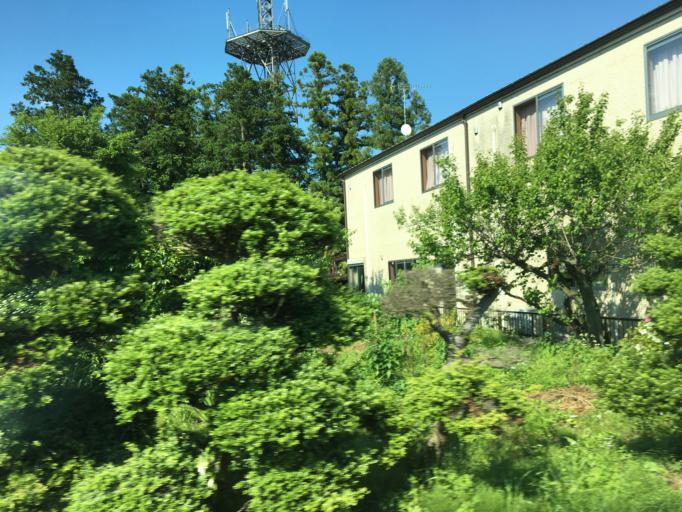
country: JP
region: Saitama
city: Morohongo
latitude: 35.9766
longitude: 139.3365
